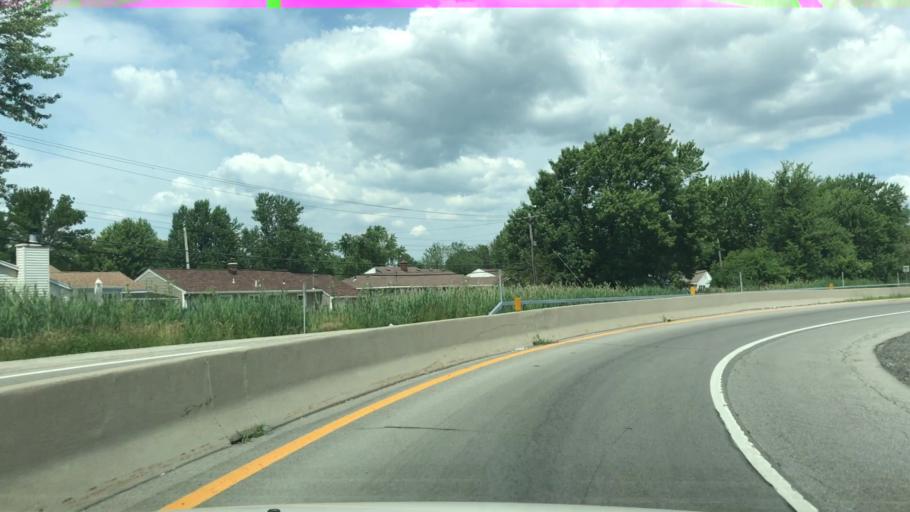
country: US
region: New York
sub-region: Erie County
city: Amherst
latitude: 42.9845
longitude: -78.7963
